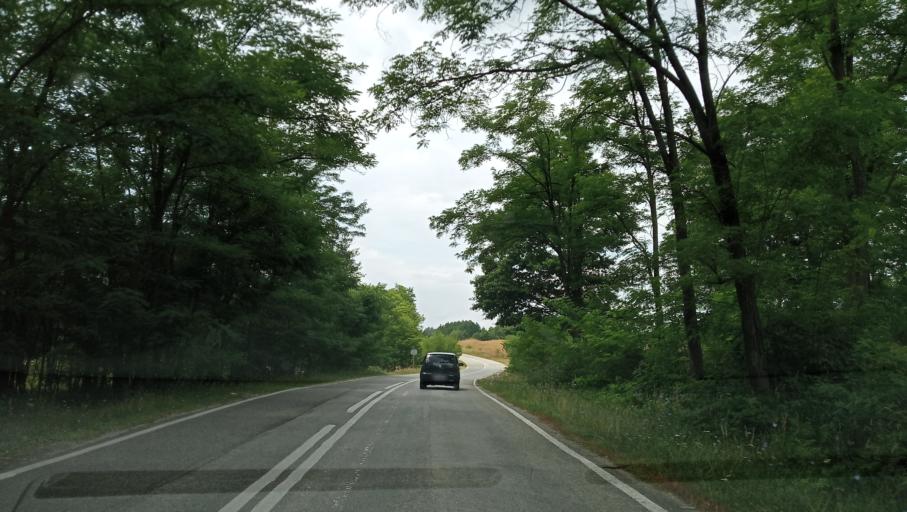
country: RO
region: Gorj
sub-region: Comuna Tismana
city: Tismana
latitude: 45.0389
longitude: 22.9803
